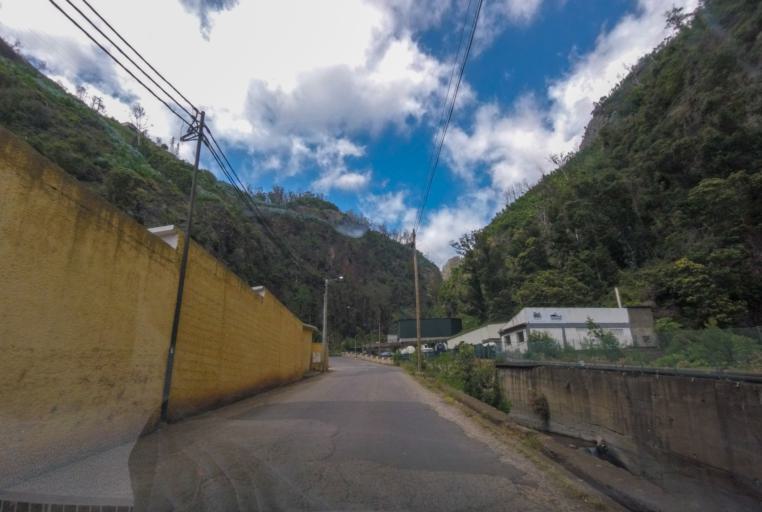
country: PT
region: Madeira
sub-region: Funchal
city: Nossa Senhora do Monte
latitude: 32.6764
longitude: -16.9179
